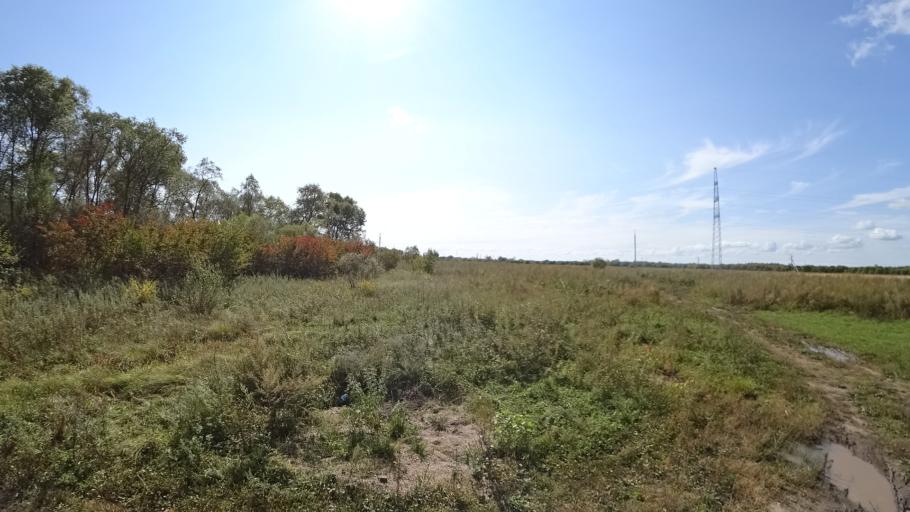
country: RU
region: Amur
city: Arkhara
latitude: 49.4001
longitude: 130.1211
